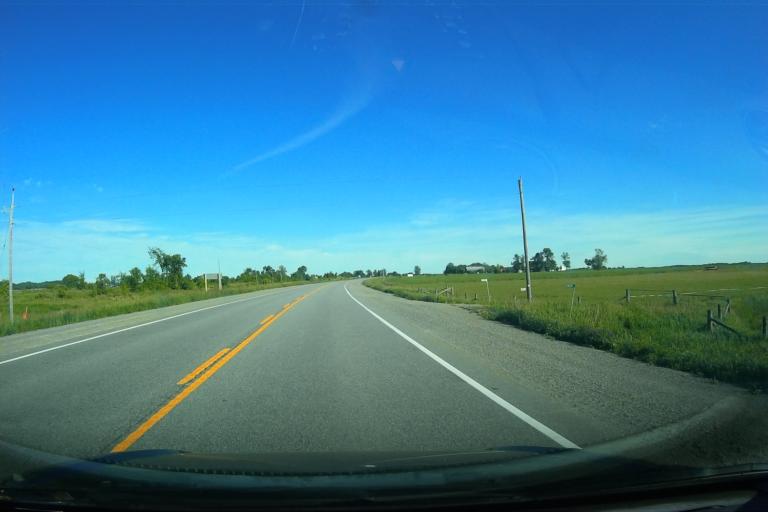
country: CA
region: Ontario
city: Pembroke
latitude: 45.6786
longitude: -76.9394
